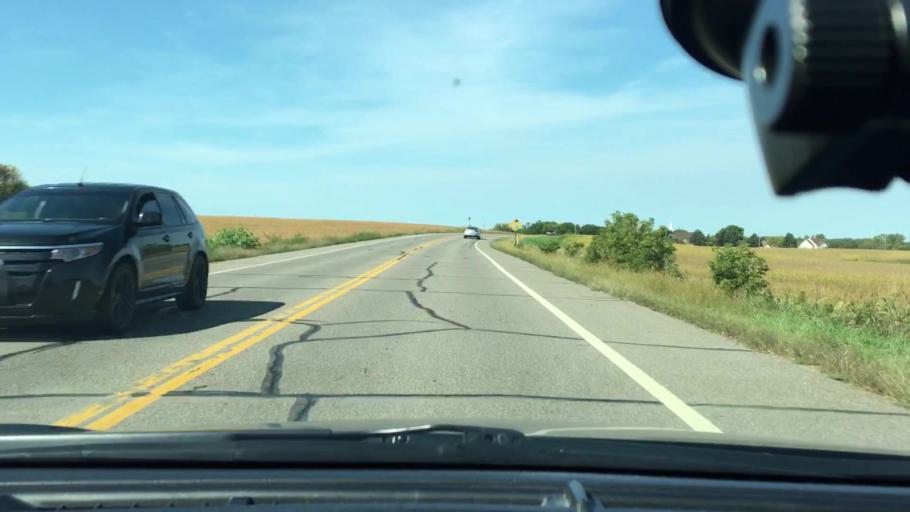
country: US
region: Minnesota
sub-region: Hennepin County
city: Corcoran
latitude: 45.0914
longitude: -93.5374
